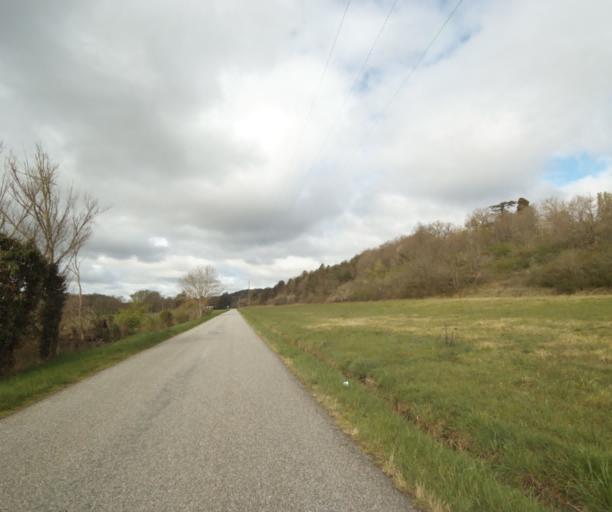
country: FR
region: Midi-Pyrenees
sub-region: Departement de l'Ariege
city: Saverdun
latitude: 43.2271
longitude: 1.5505
